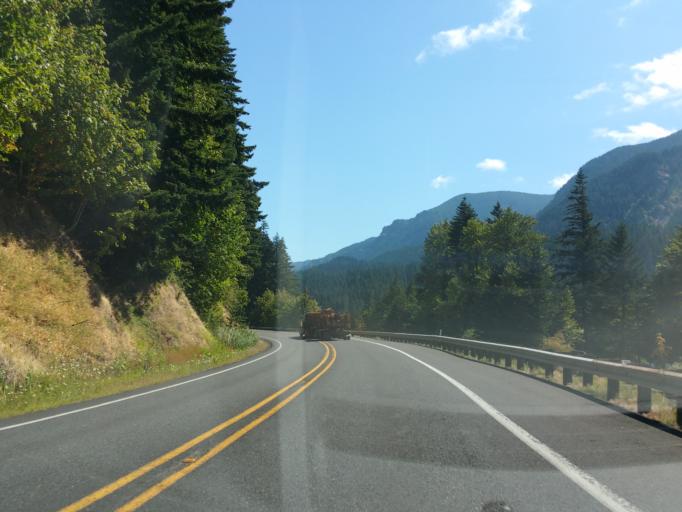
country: US
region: Oregon
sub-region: Hood River County
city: Cascade Locks
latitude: 45.6536
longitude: -121.9154
